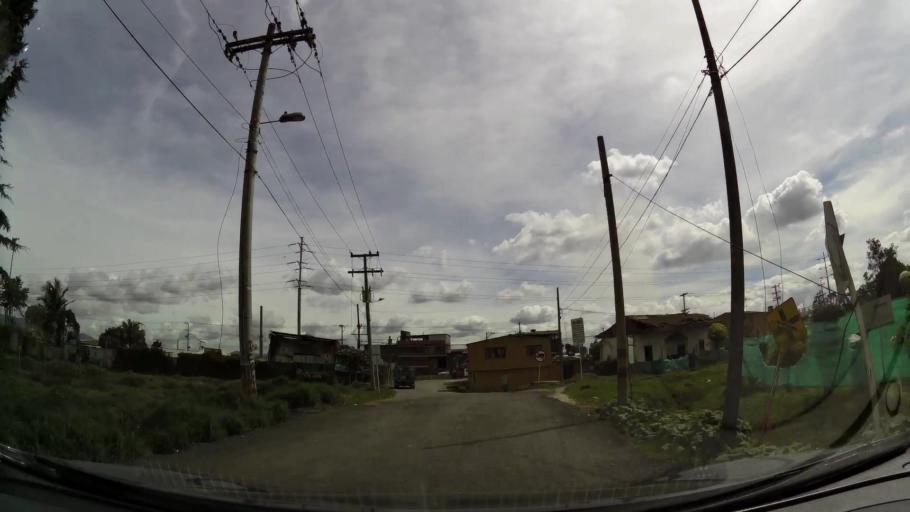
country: CO
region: Cundinamarca
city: Funza
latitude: 4.6998
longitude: -74.1813
